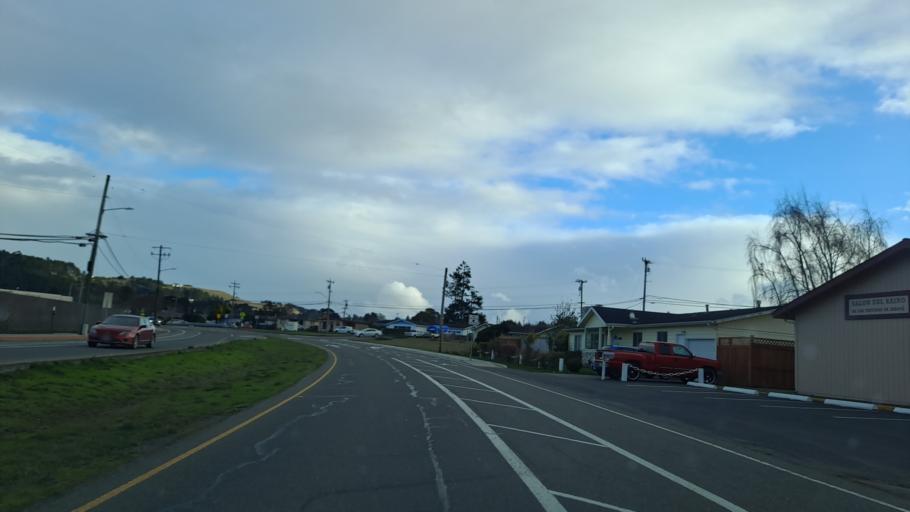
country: US
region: California
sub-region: Humboldt County
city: Fortuna
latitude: 40.5711
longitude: -124.1408
